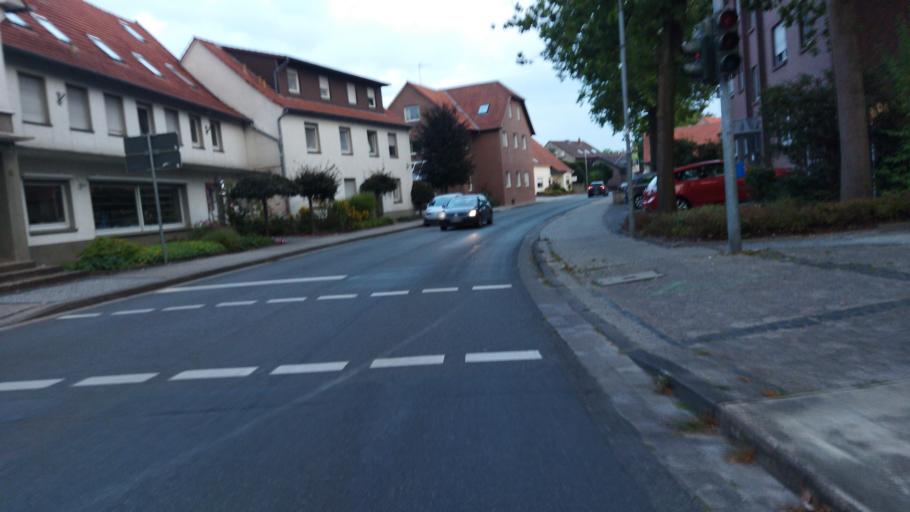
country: DE
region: Lower Saxony
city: Bad Laer
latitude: 52.1041
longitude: 8.0862
